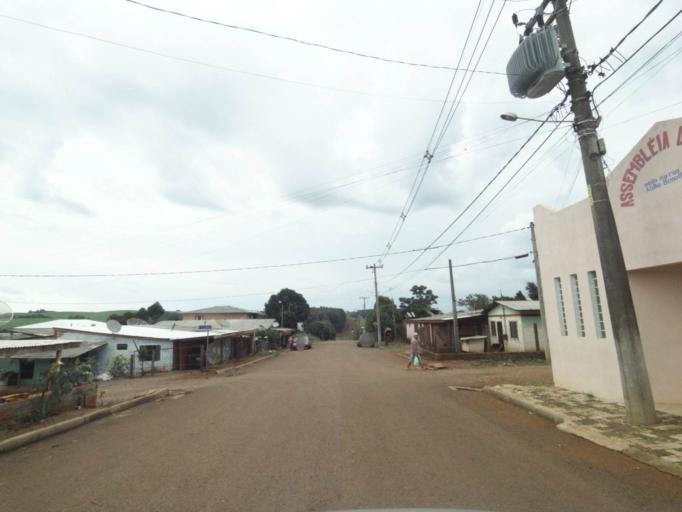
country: BR
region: Rio Grande do Sul
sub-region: Lagoa Vermelha
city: Lagoa Vermelha
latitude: -28.2290
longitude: -51.5167
